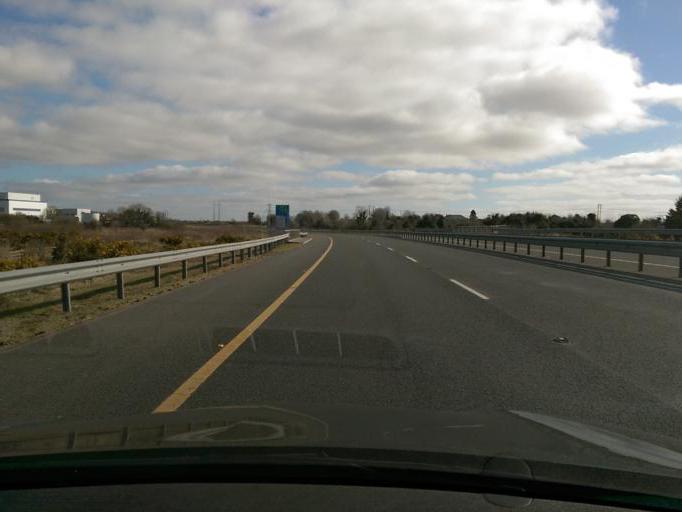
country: IE
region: Leinster
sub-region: An Iarmhi
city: Athlone
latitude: 53.4149
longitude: -7.9941
